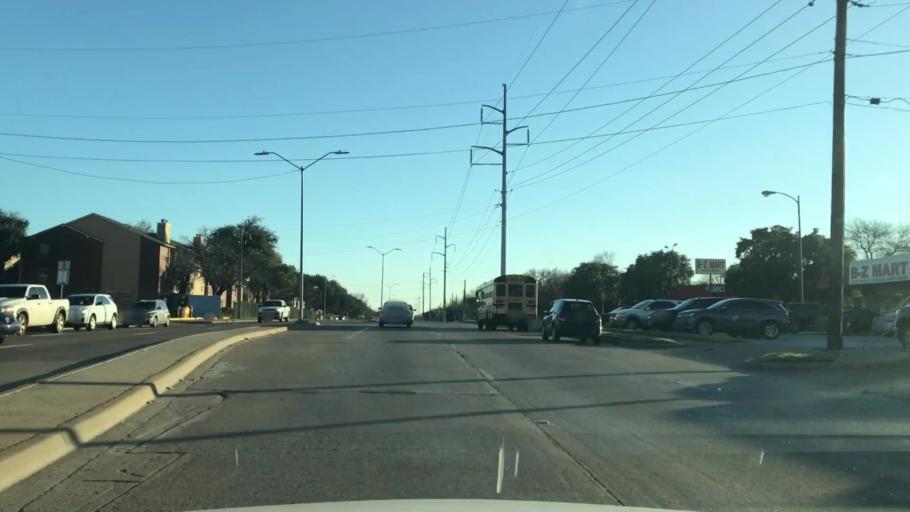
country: US
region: Texas
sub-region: Dallas County
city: Balch Springs
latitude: 32.7915
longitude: -96.7001
